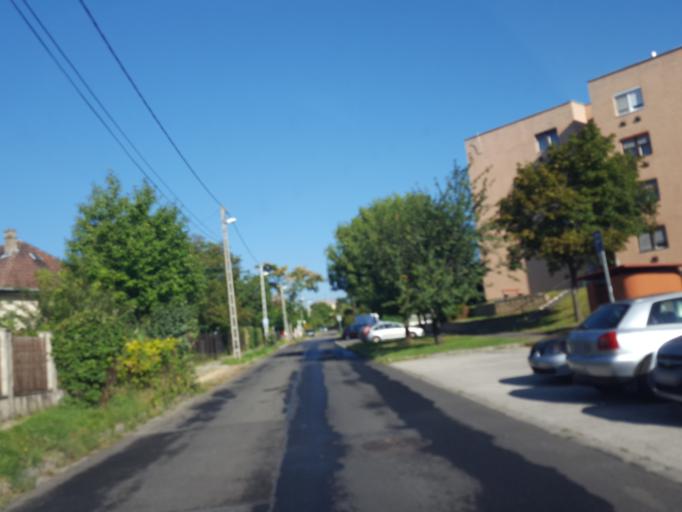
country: HU
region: Budapest
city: Budapest XXII. keruelet
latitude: 47.4273
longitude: 19.0211
